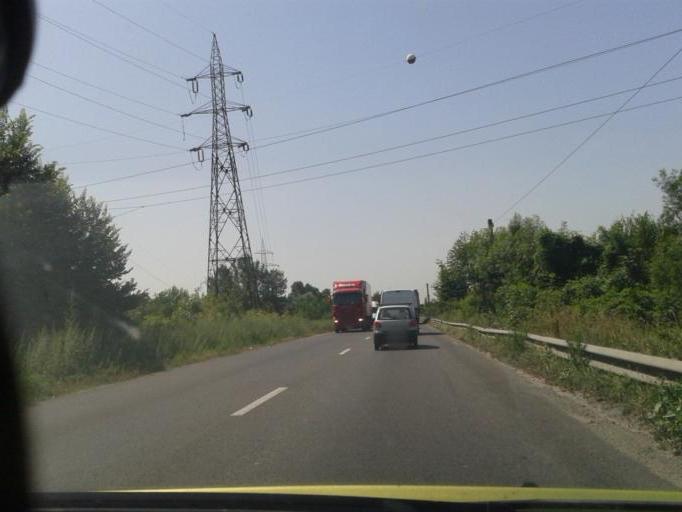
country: RO
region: Ilfov
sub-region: Comuna Pantelimon
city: Pantelimon
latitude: 44.4412
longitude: 26.2353
